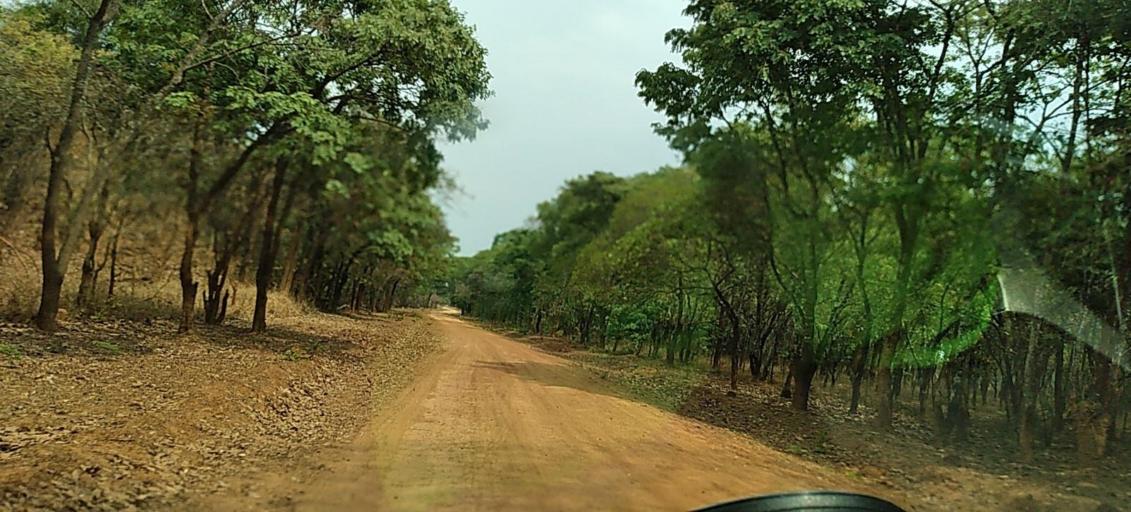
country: ZM
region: North-Western
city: Solwezi
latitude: -12.9543
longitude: 26.5639
